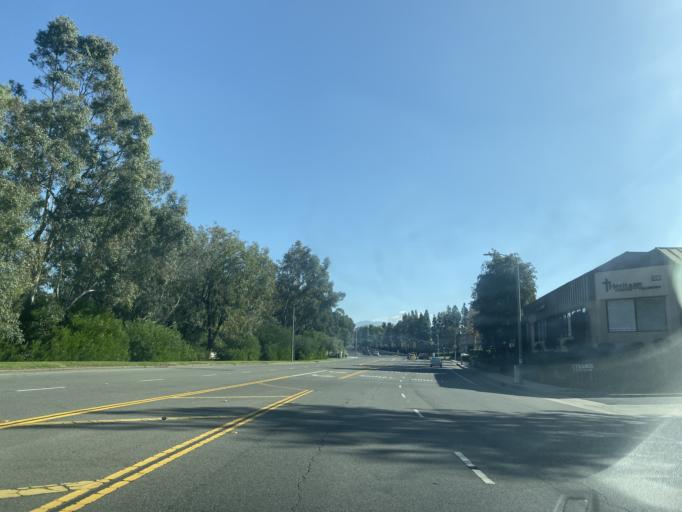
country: US
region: California
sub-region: Orange County
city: North Tustin
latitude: 33.7958
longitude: -117.7734
